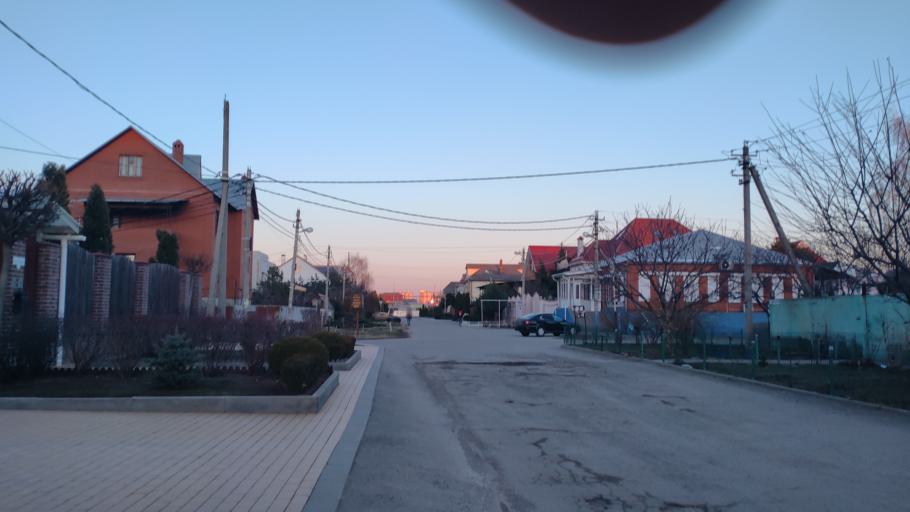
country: RU
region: Krasnodarskiy
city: Krasnodar
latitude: 45.0751
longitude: 39.0118
